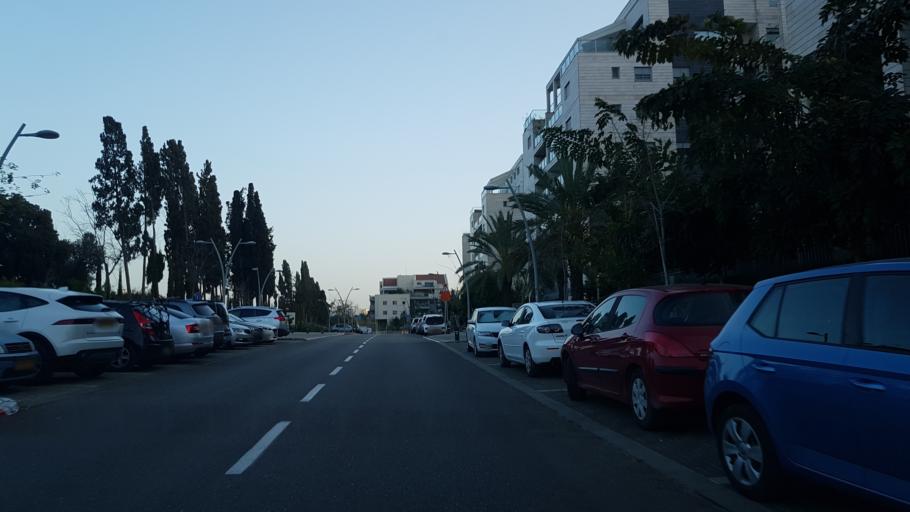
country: IL
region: Central District
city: Kfar Saba
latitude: 32.1969
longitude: 34.8970
